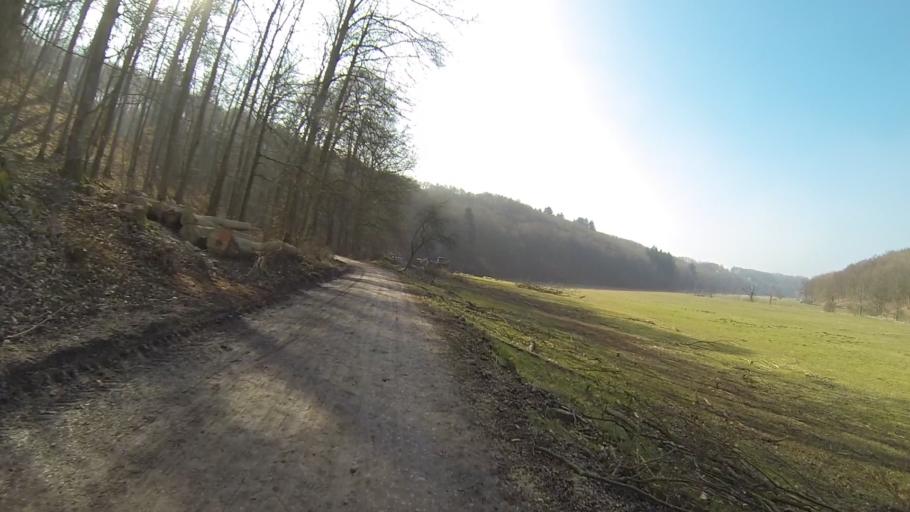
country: DE
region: Baden-Wuerttemberg
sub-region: Regierungsbezirk Stuttgart
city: Herbrechtingen
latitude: 48.5972
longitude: 10.1766
